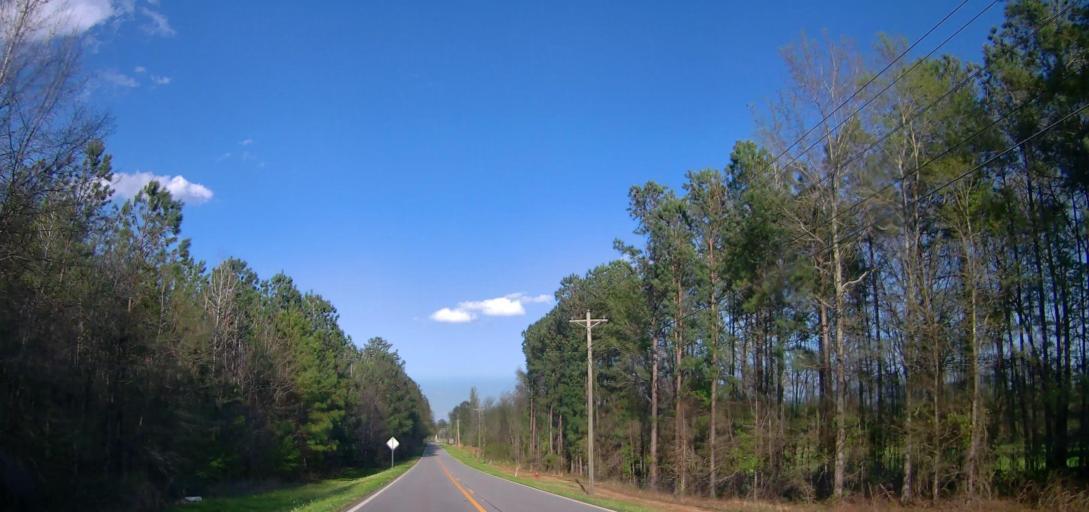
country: US
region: Georgia
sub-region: Putnam County
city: Eatonton
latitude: 33.1967
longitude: -83.3923
